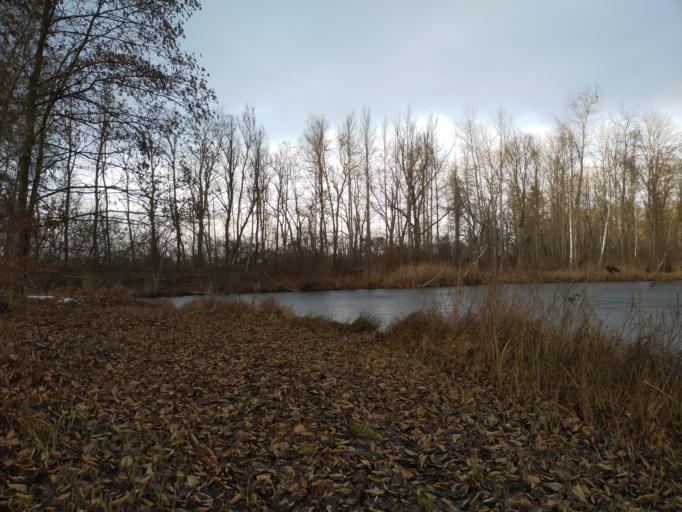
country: DE
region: Bavaria
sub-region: Swabia
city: Guenzburg
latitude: 48.4803
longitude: 10.3129
